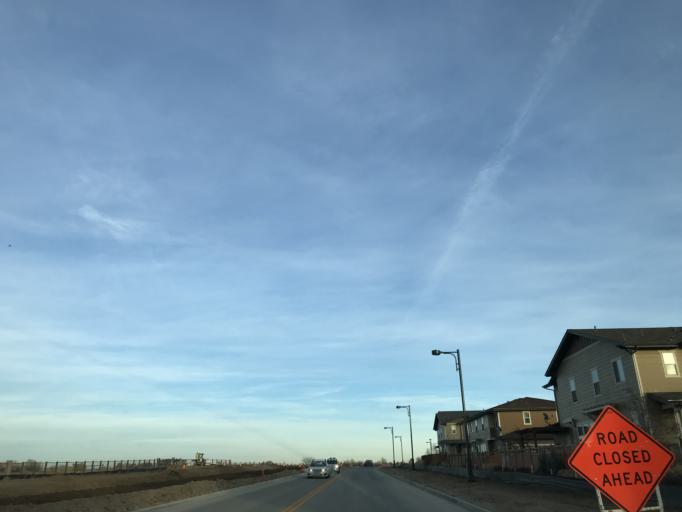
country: US
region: Colorado
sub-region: Adams County
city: Aurora
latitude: 39.7575
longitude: -104.8585
